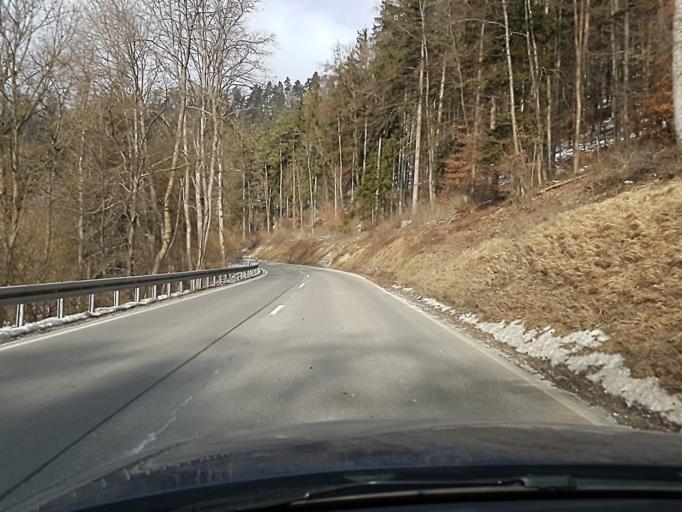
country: DE
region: Baden-Wuerttemberg
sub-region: Freiburg Region
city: Muhlheim am Bach
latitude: 48.3967
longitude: 8.6663
